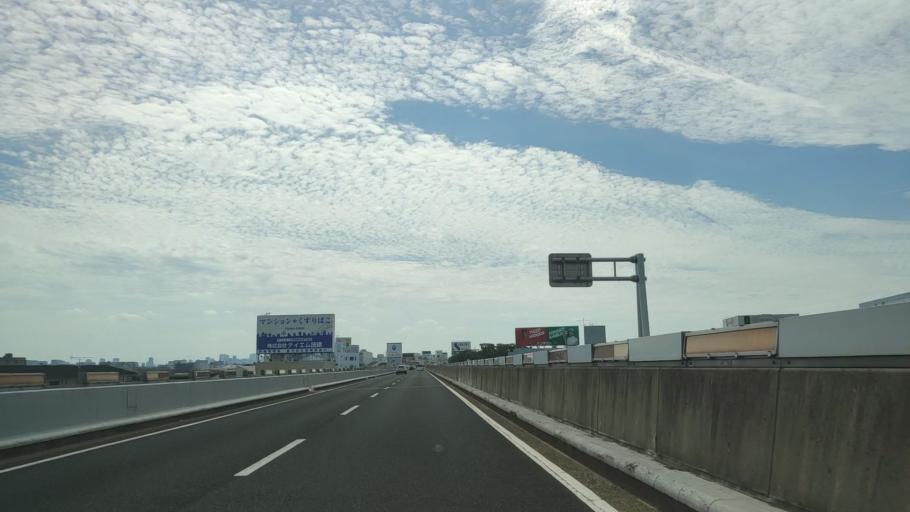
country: JP
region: Osaka
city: Toyonaka
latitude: 34.7687
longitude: 135.4598
